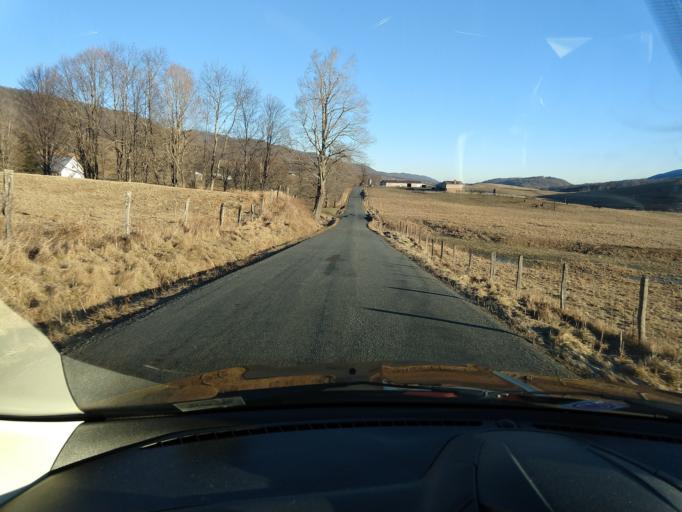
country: US
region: Virginia
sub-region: Highland County
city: Monterey
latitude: 38.3814
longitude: -79.6636
